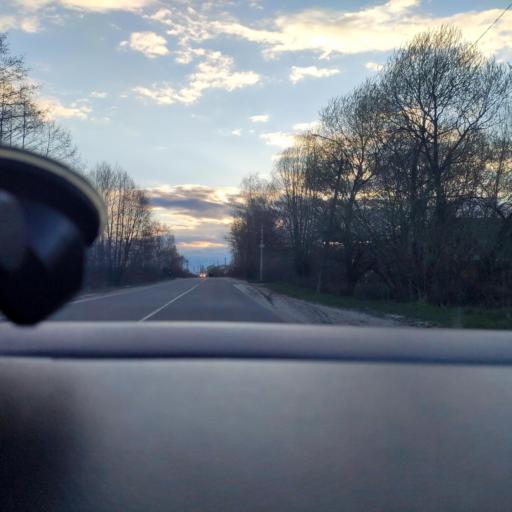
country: RU
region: Moskovskaya
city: Krasnyy Tkach
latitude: 55.4286
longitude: 39.2063
